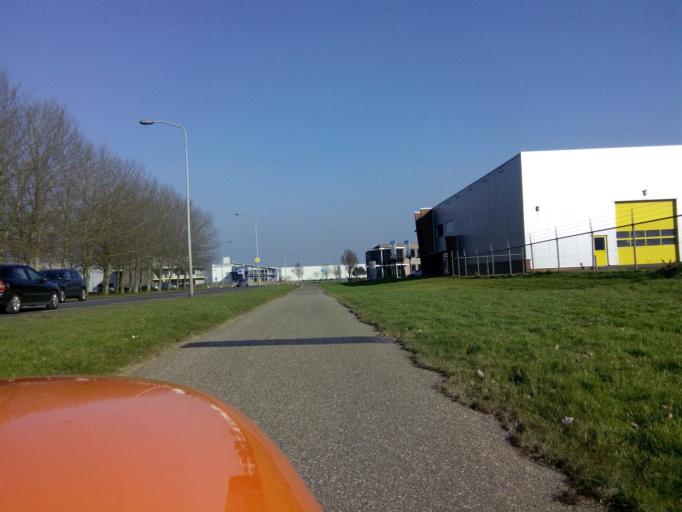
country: NL
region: Flevoland
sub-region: Gemeente Zeewolde
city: Zeewolde
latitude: 52.3520
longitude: 5.5000
